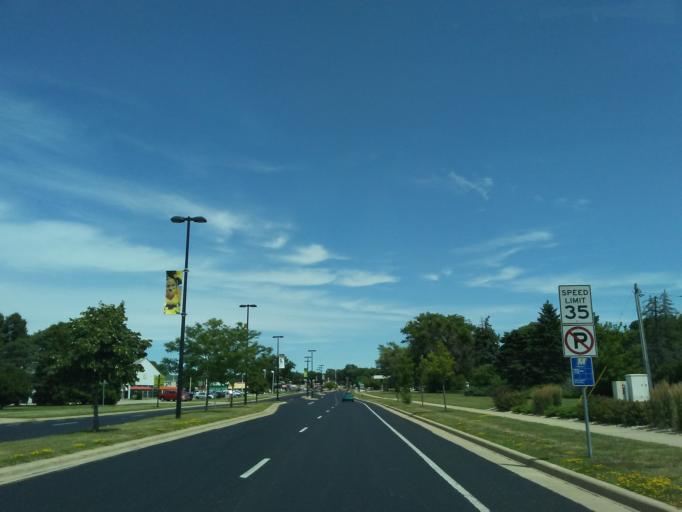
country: US
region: Wisconsin
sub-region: Dane County
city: Middleton
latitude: 43.1062
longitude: -89.5106
